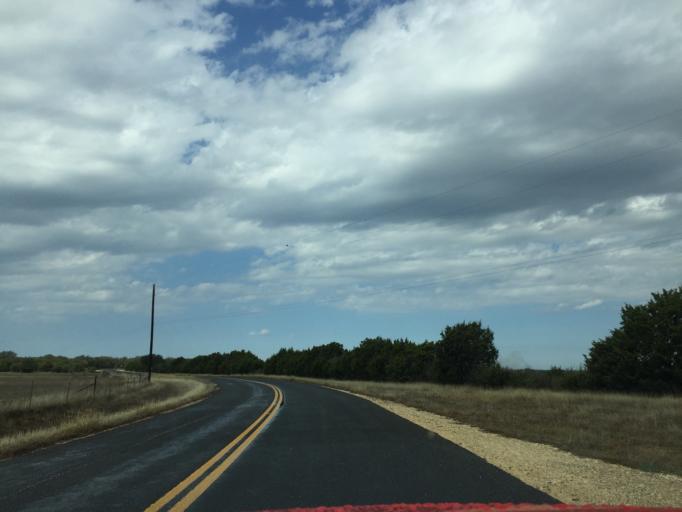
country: US
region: Texas
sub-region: Burnet County
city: Bertram
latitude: 30.6278
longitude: -97.9916
